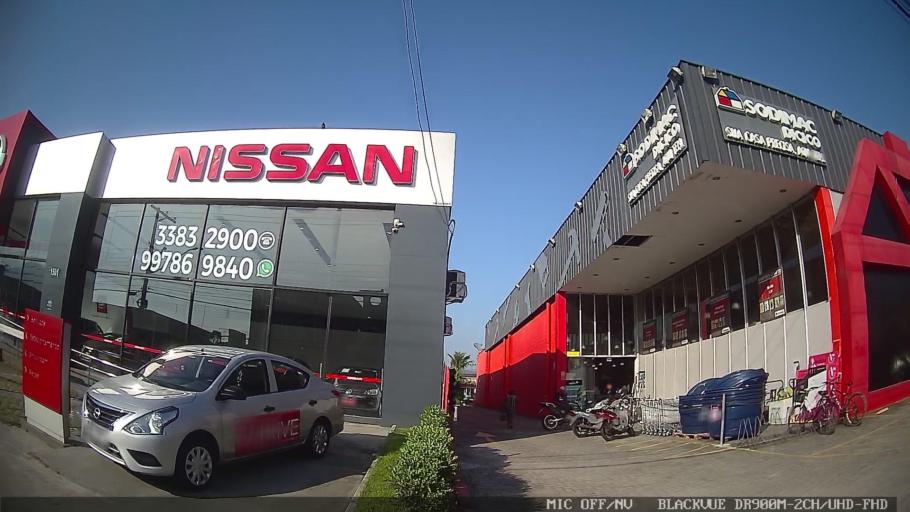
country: BR
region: Sao Paulo
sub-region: Guaruja
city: Guaruja
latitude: -23.9919
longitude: -46.2745
